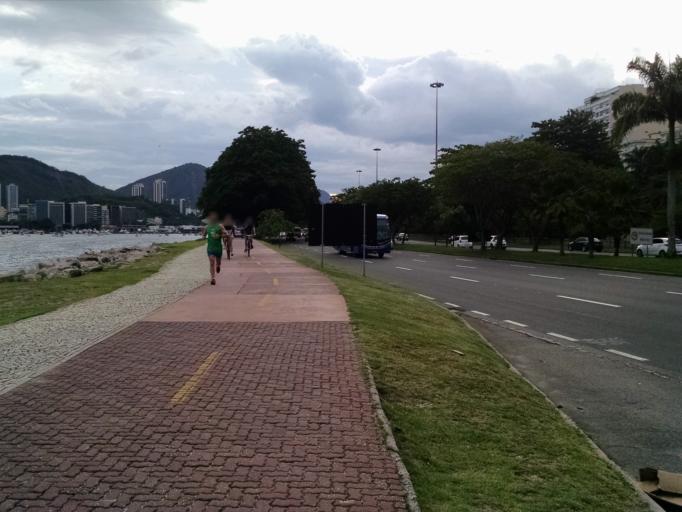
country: BR
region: Rio de Janeiro
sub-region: Rio De Janeiro
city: Rio de Janeiro
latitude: -22.9413
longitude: -43.1708
